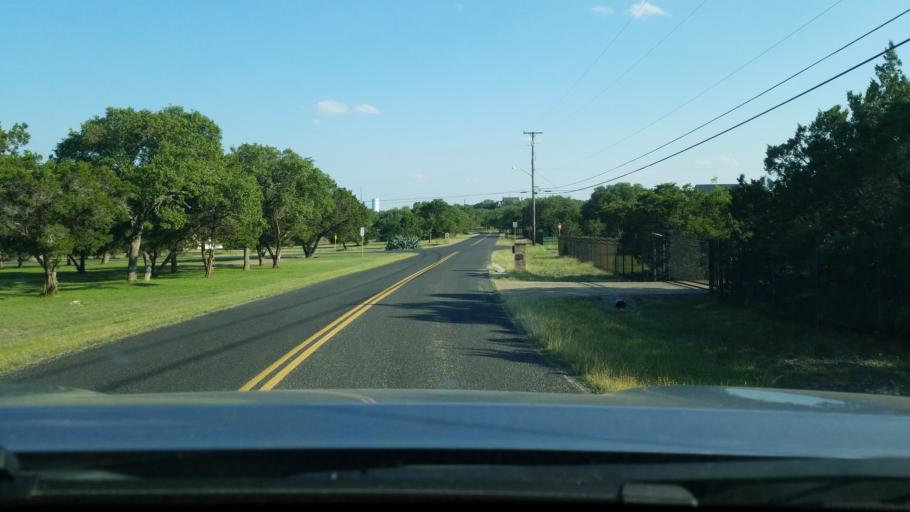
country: US
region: Texas
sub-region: Bexar County
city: Timberwood Park
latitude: 29.7059
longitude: -98.4377
